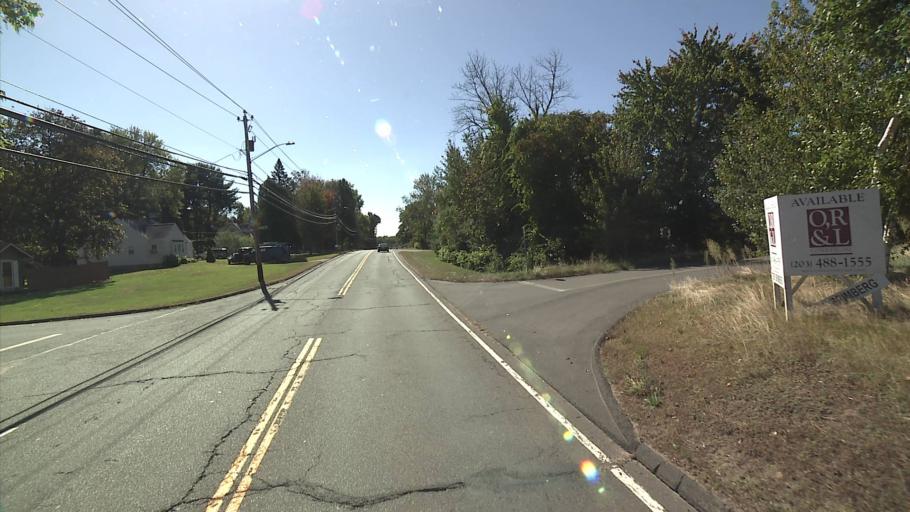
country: US
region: Connecticut
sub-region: New Haven County
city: Wolcott
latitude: 41.6333
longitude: -72.9630
